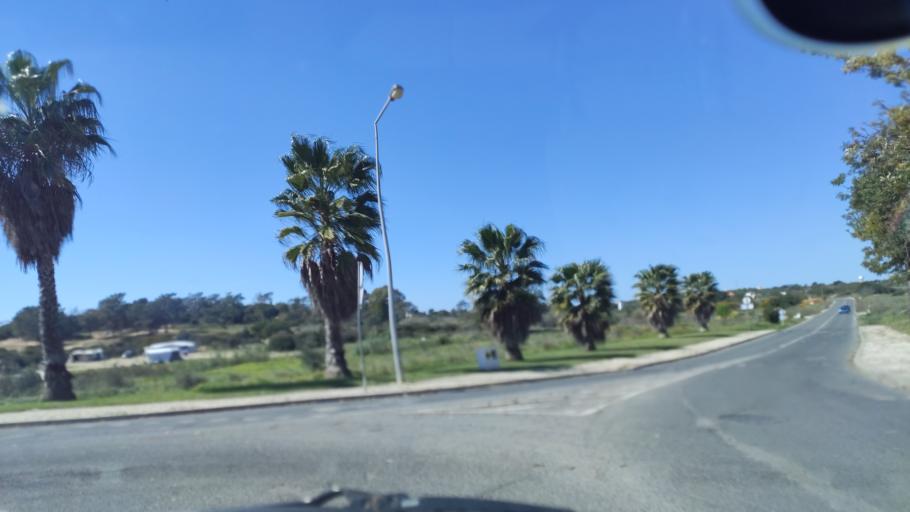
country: PT
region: Faro
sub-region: Olhao
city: Olhao
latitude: 37.0408
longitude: -7.8518
